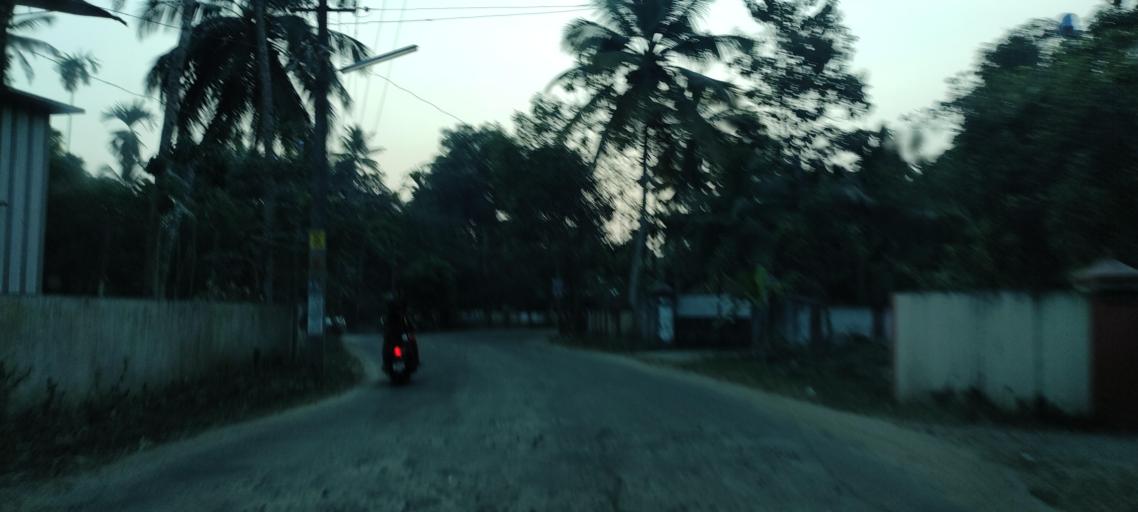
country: IN
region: Kerala
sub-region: Alappuzha
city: Kayankulam
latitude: 9.1207
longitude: 76.4920
